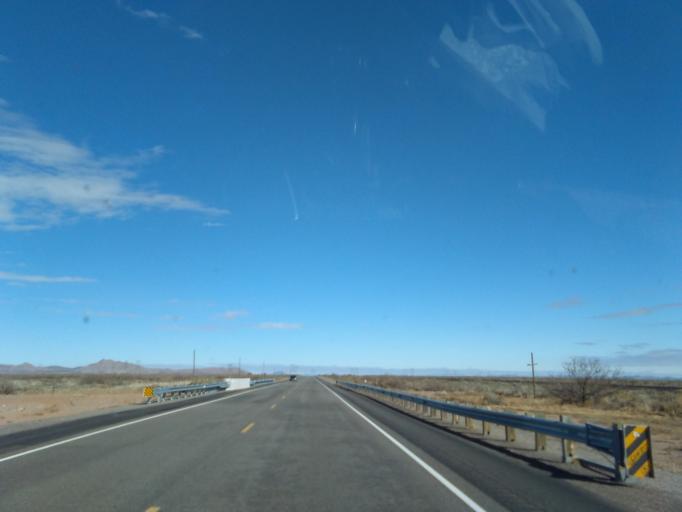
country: US
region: New Mexico
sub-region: Luna County
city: Deming
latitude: 32.3070
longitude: -107.6972
